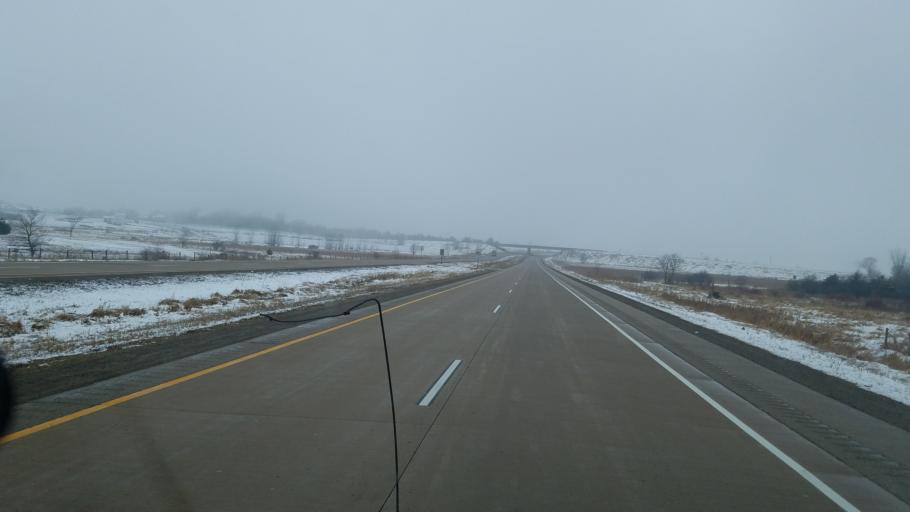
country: US
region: Wisconsin
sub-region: Winnebago County
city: Winneconne
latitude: 44.1293
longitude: -88.6576
